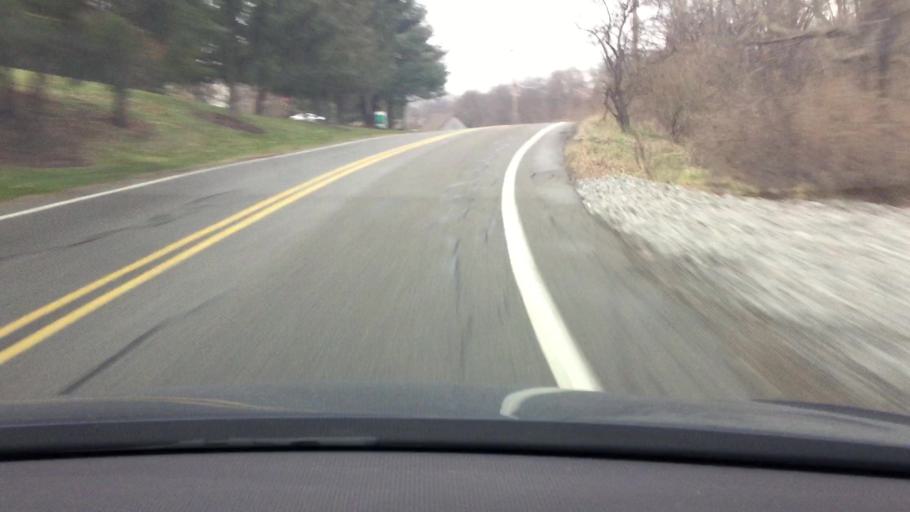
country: US
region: Pennsylvania
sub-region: Allegheny County
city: Rennerdale
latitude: 40.4422
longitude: -80.1393
